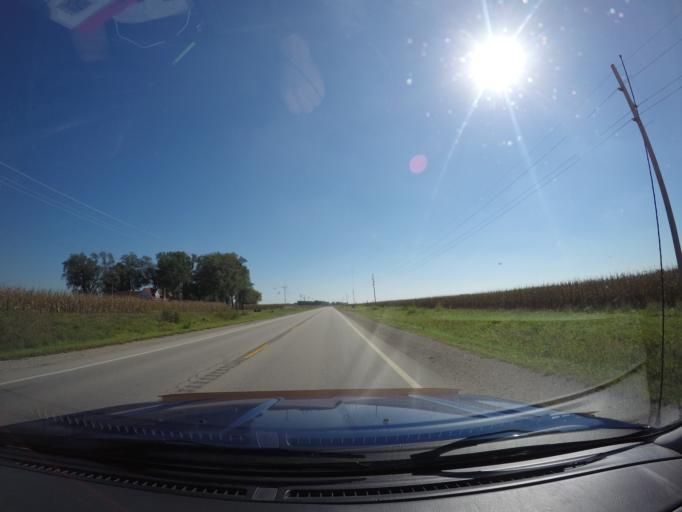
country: US
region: Kansas
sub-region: Shawnee County
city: Silver Lake
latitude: 39.0939
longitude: -95.8141
